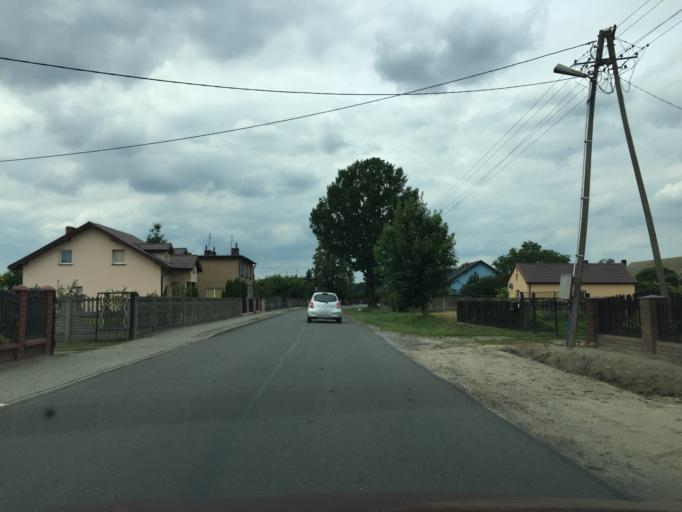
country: PL
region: Greater Poland Voivodeship
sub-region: Powiat kaliski
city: Stawiszyn
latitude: 51.9443
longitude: 18.1869
